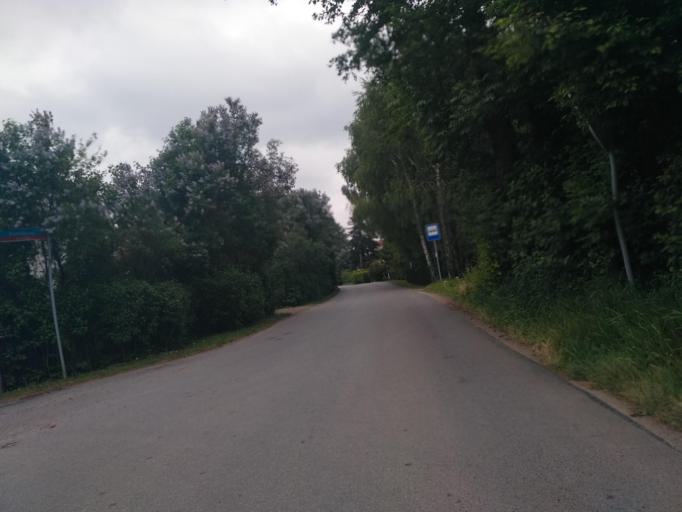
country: PL
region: Subcarpathian Voivodeship
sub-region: Krosno
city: Krosno
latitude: 49.6754
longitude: 21.7343
